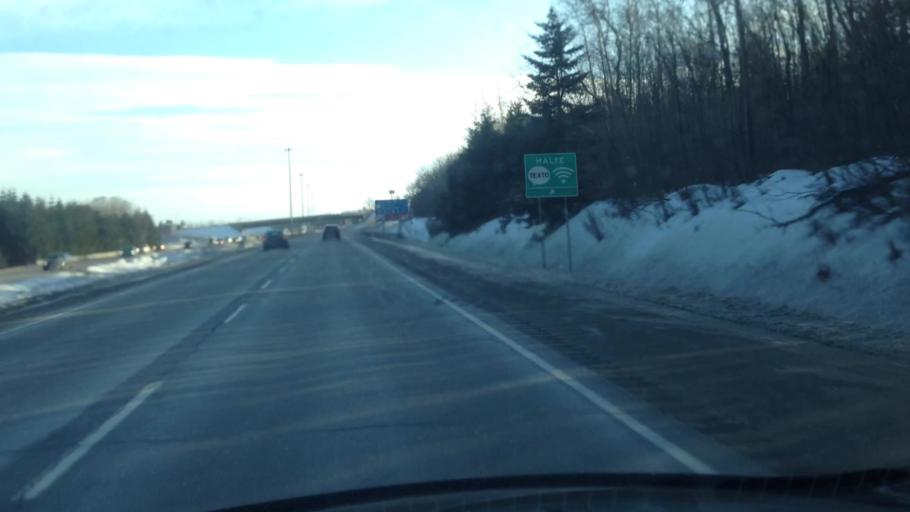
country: CA
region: Quebec
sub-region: Laurentides
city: Prevost
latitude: 45.8468
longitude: -74.0724
